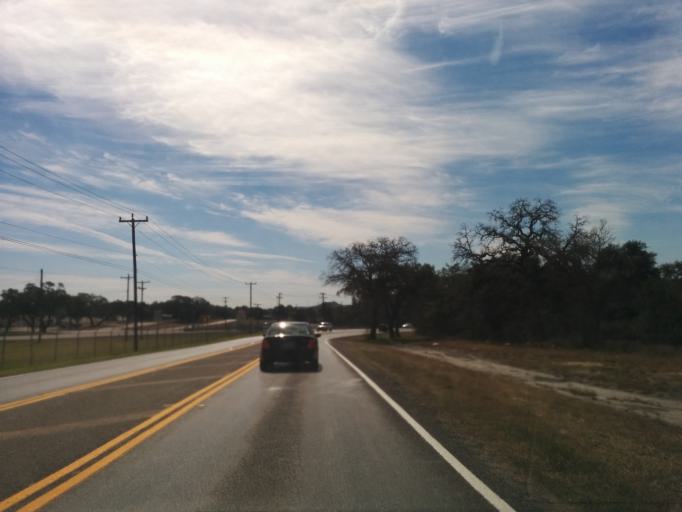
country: US
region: Texas
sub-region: Bexar County
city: Cross Mountain
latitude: 29.6807
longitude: -98.6315
